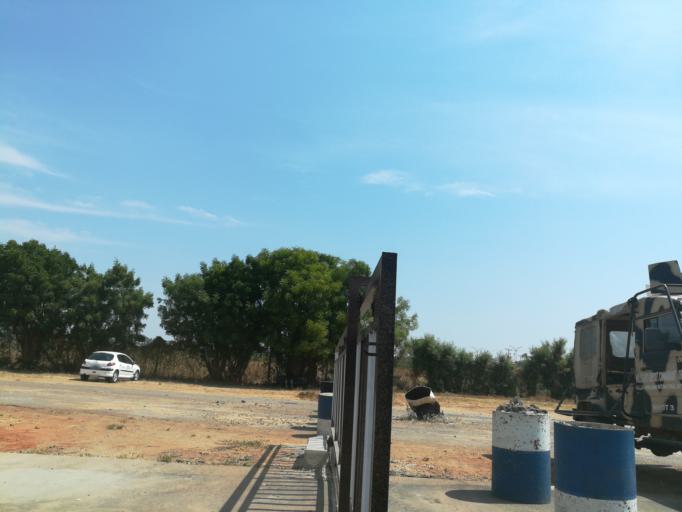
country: NG
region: Kano
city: Kano
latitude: 12.0341
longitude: 8.5161
